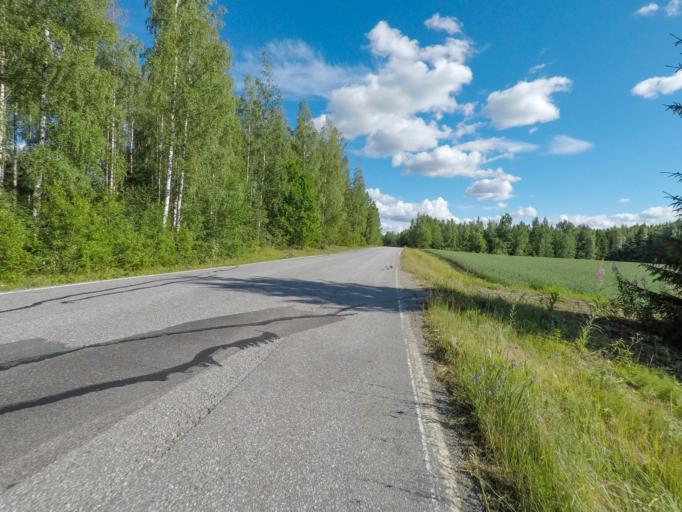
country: FI
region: South Karelia
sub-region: Imatra
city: Imatra
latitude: 61.1333
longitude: 28.6604
